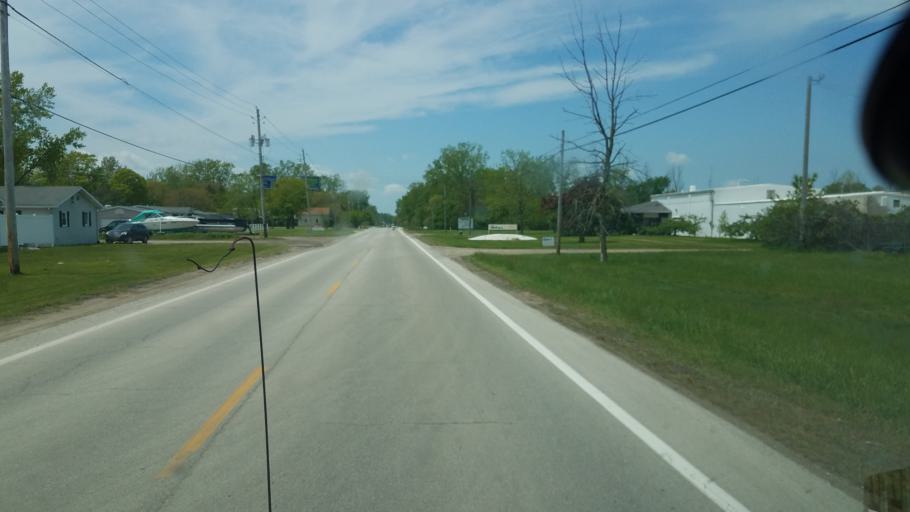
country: US
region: Ohio
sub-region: Ottawa County
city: Port Clinton
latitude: 41.5210
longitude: -82.9751
